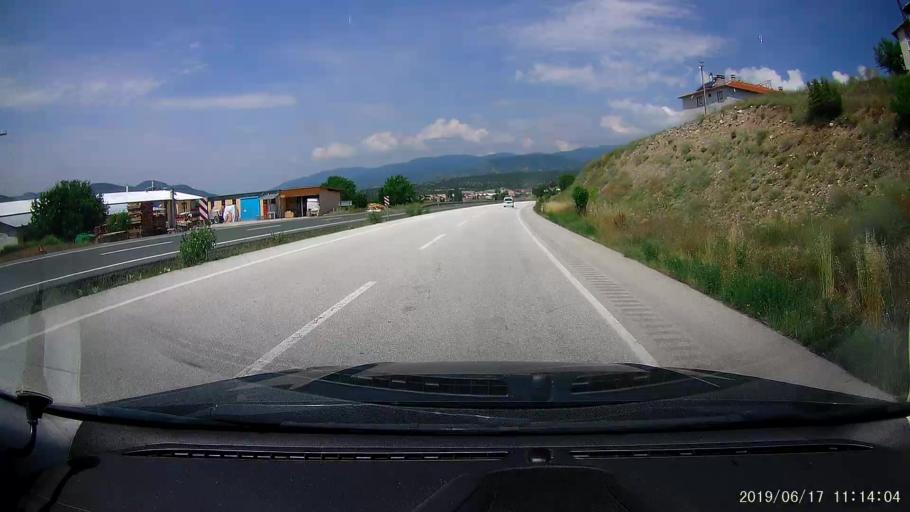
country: TR
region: Kastamonu
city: Tosya
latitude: 40.9567
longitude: 33.9576
